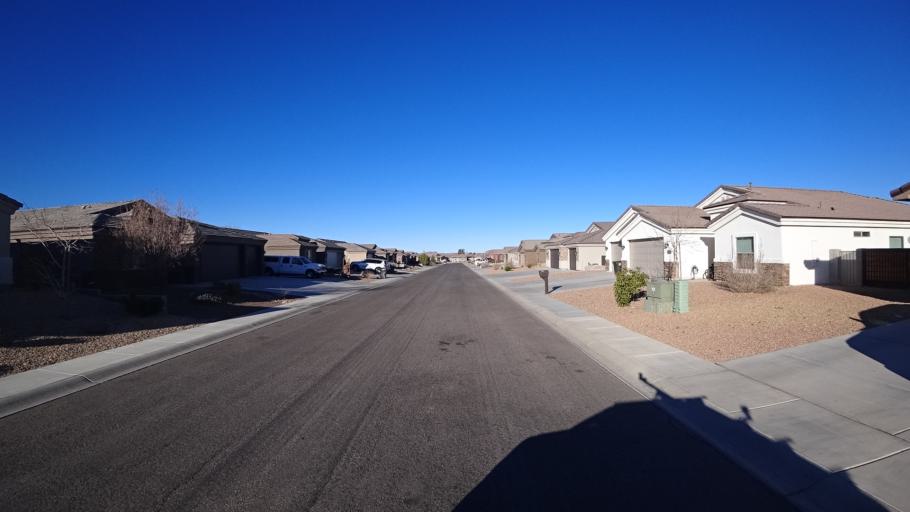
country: US
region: Arizona
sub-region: Mohave County
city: Kingman
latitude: 35.1929
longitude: -113.9994
